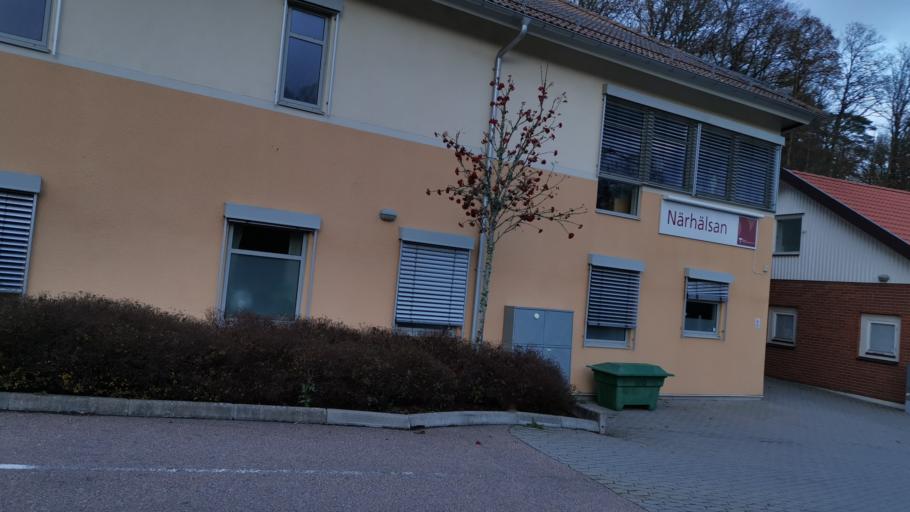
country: SE
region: Vaestra Goetaland
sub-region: Munkedals Kommun
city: Munkedal
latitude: 58.4677
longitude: 11.6677
